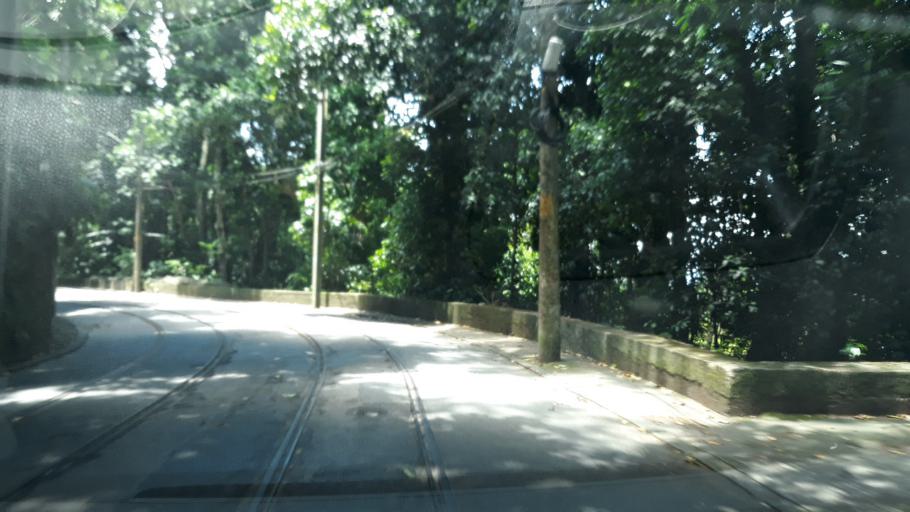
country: BR
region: Rio de Janeiro
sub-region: Rio De Janeiro
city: Rio de Janeiro
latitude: -22.9410
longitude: -43.2105
